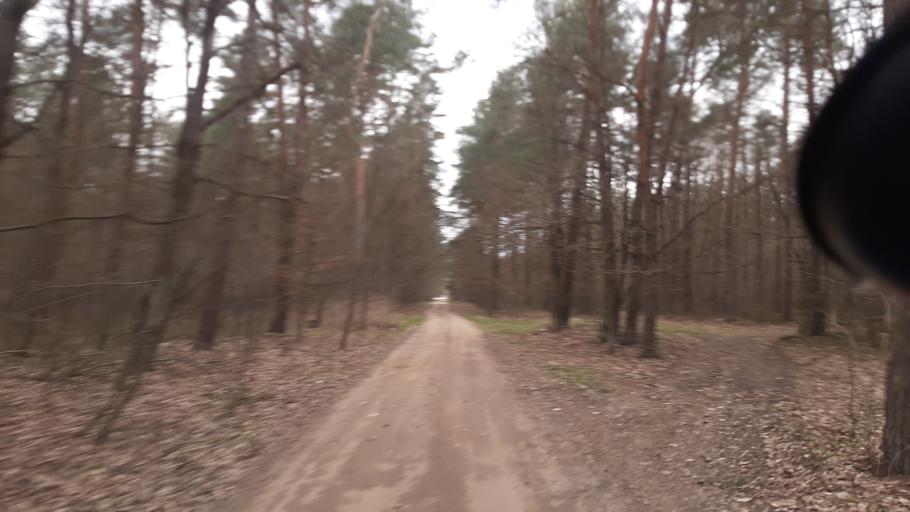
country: PL
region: Lublin Voivodeship
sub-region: Powiat lubartowski
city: Abramow
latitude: 51.4439
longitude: 22.3433
